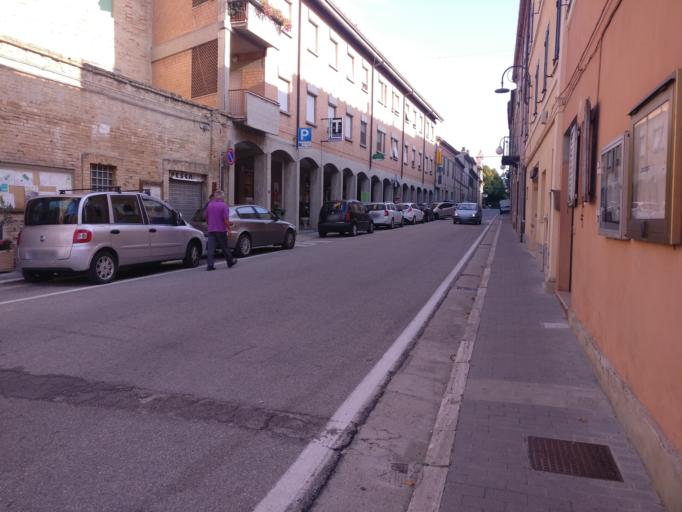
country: IT
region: The Marches
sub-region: Provincia di Ascoli Piceno
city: Montalto delle Marche
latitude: 42.9889
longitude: 13.6086
